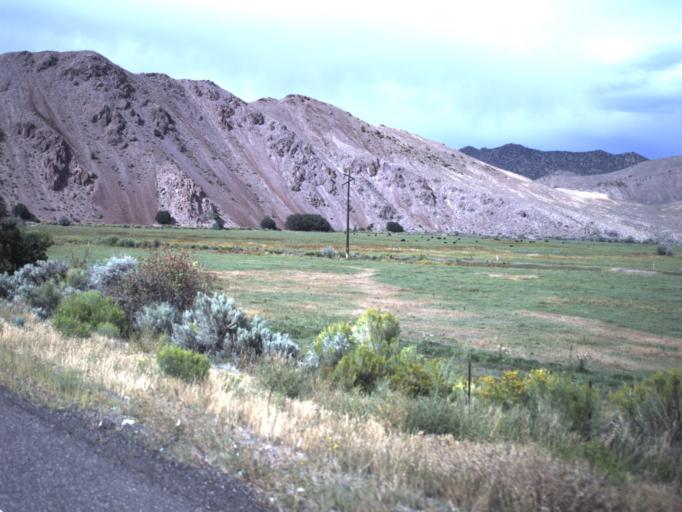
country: US
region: Utah
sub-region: Sevier County
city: Monroe
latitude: 38.4753
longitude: -112.2387
